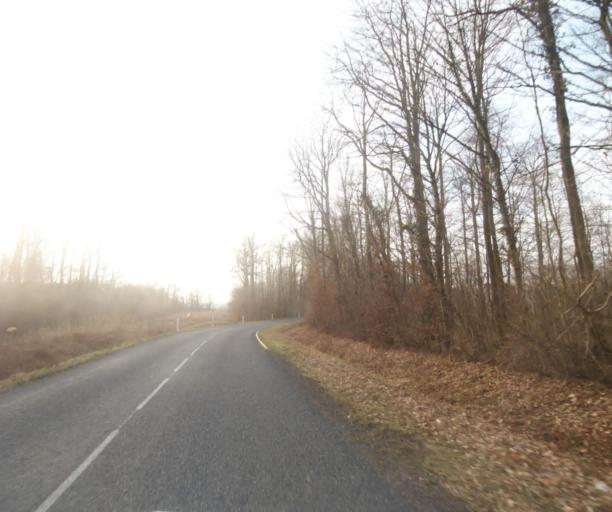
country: FR
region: Champagne-Ardenne
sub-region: Departement de la Haute-Marne
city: Bettancourt-la-Ferree
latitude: 48.6624
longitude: 4.9448
